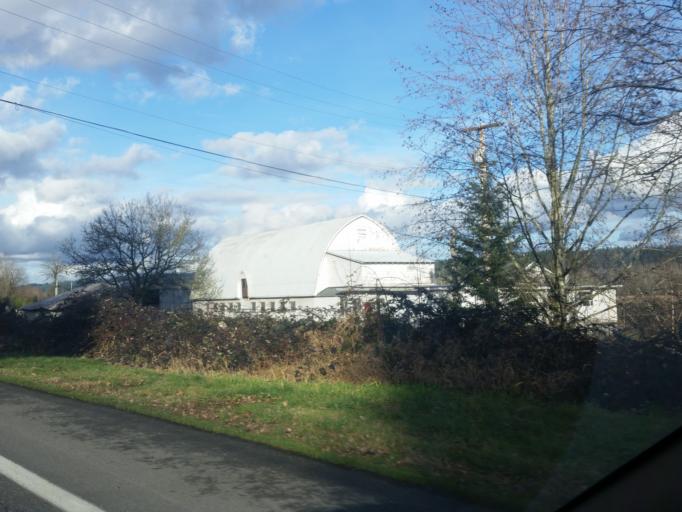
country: US
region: Washington
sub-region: King County
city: Kingsgate
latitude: 47.7093
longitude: -122.1542
